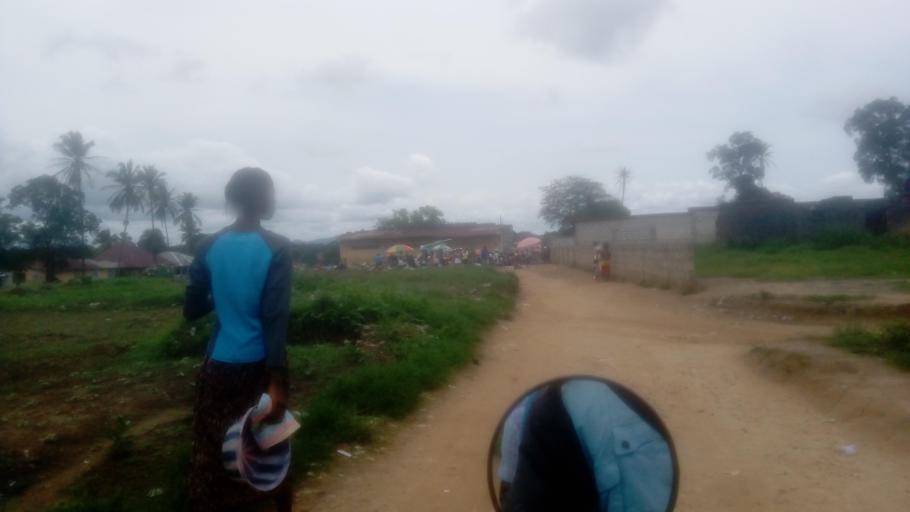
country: SL
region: Southern Province
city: Bo
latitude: 7.9411
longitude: -11.7295
